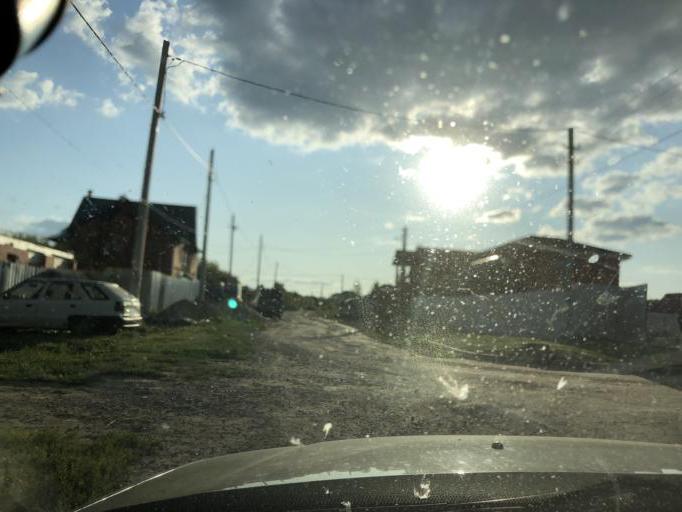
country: RU
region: Tula
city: Kosaya Gora
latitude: 54.1738
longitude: 37.5459
